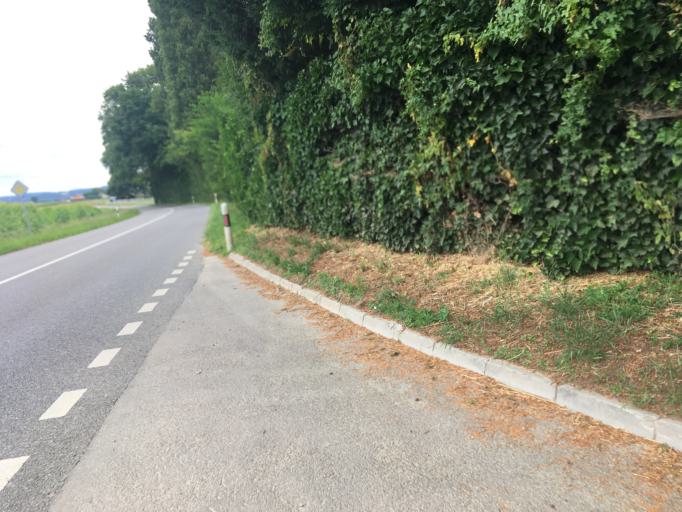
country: CH
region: Vaud
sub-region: Broye-Vully District
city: Payerne
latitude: 46.8757
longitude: 6.9556
